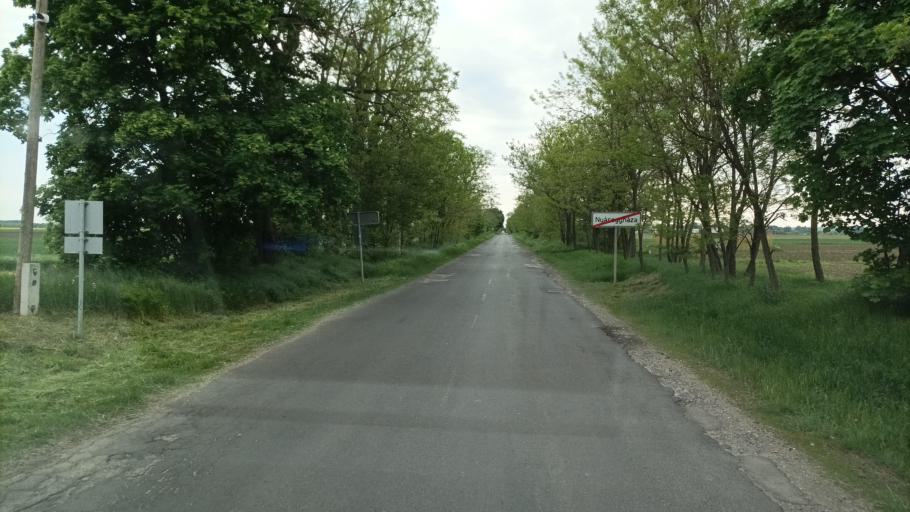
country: HU
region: Pest
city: Nyaregyhaza
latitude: 47.2659
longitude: 19.5134
